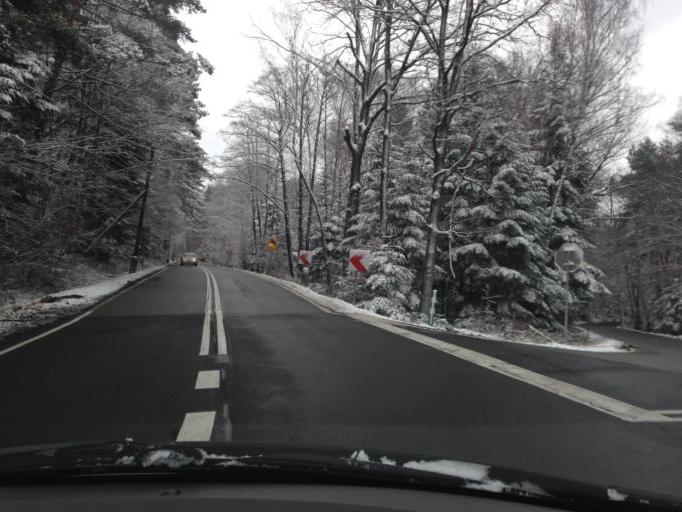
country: PL
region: Lesser Poland Voivodeship
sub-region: Powiat bochenski
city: Nowy Wisnicz
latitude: 49.8520
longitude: 20.4730
